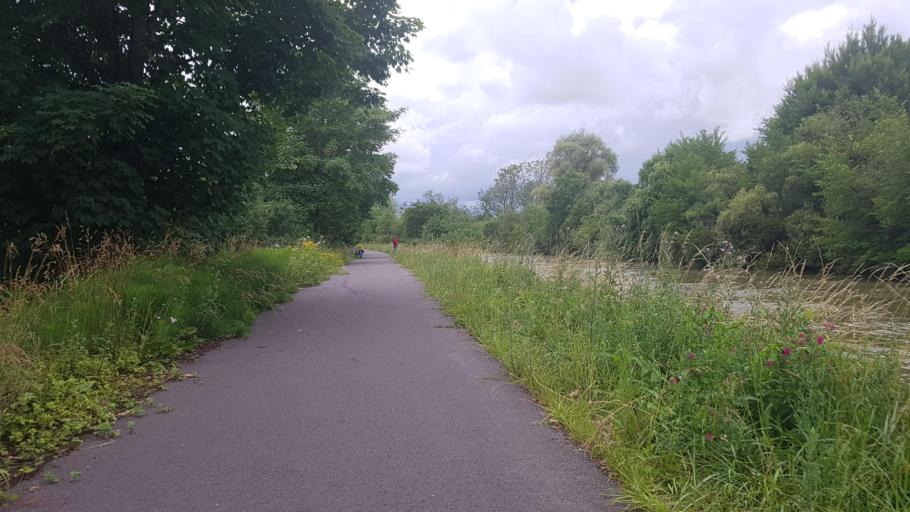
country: FR
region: Lorraine
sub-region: Departement de la Moselle
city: Dieuze
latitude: 48.6892
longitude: 6.6705
